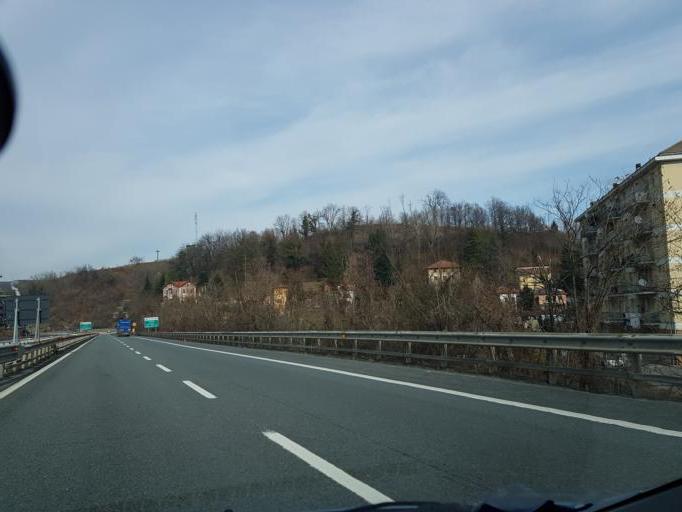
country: IT
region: Liguria
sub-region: Provincia di Genova
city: Busalla
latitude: 44.5733
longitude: 8.9502
